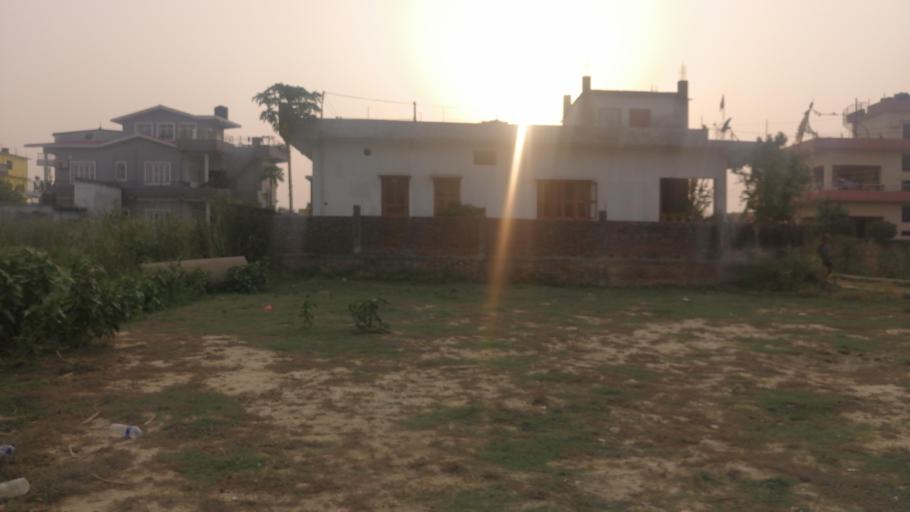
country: NP
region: Western Region
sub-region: Lumbini Zone
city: Bhairahawa
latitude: 27.5070
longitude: 83.4607
